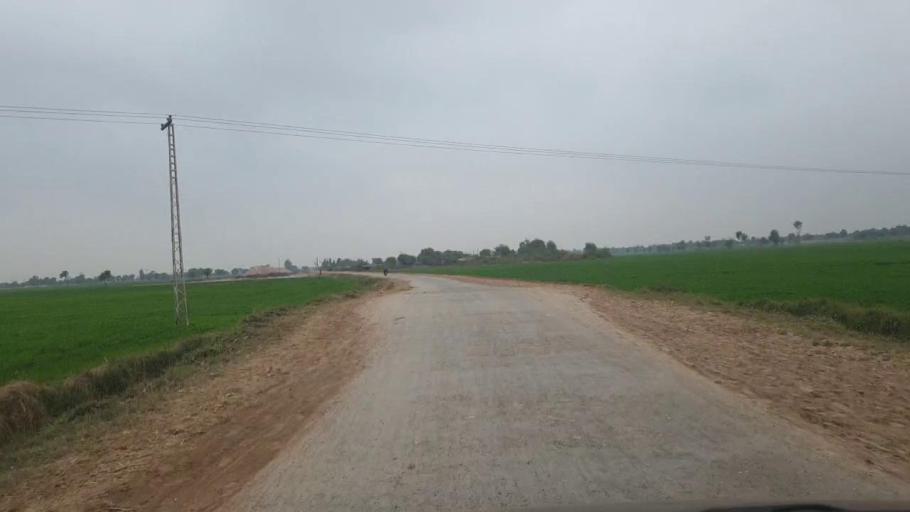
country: PK
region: Sindh
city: Shahdadpur
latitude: 25.9567
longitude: 68.7237
